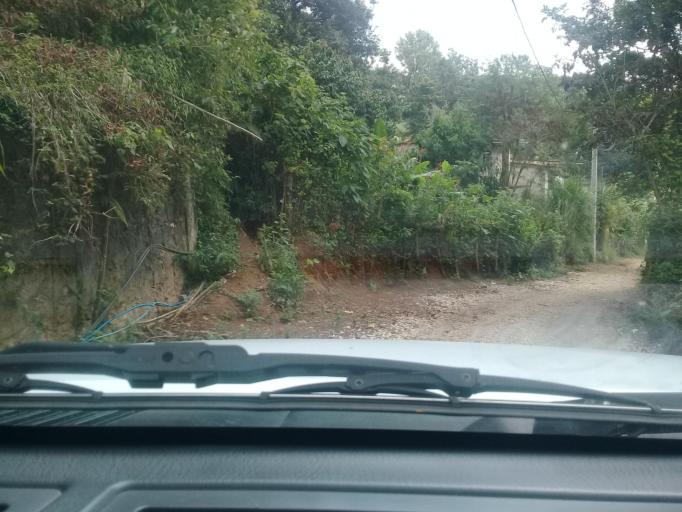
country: MX
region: Veracruz
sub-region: Tlalnelhuayocan
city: Otilpan
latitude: 19.5540
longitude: -96.9800
